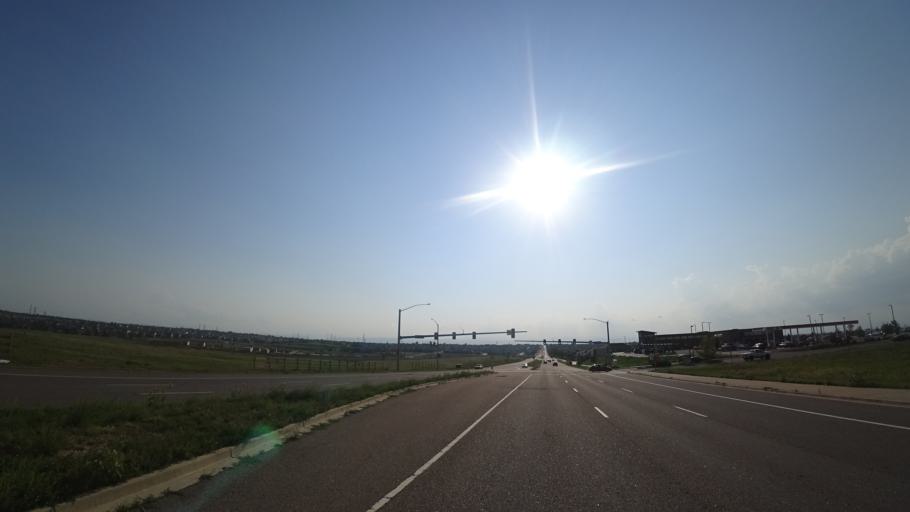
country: US
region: Colorado
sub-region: Arapahoe County
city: Dove Valley
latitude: 39.6385
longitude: -104.7364
